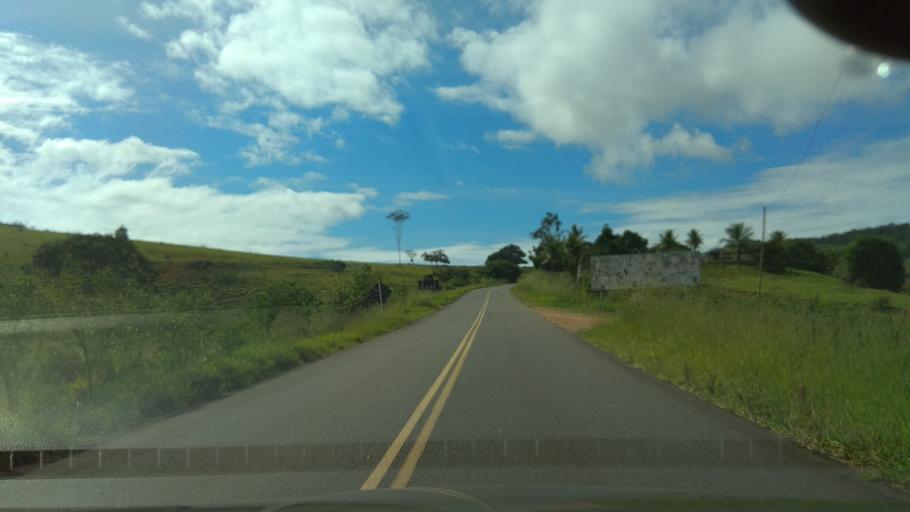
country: BR
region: Bahia
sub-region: Ubaira
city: Ubaira
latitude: -13.2627
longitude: -39.6989
